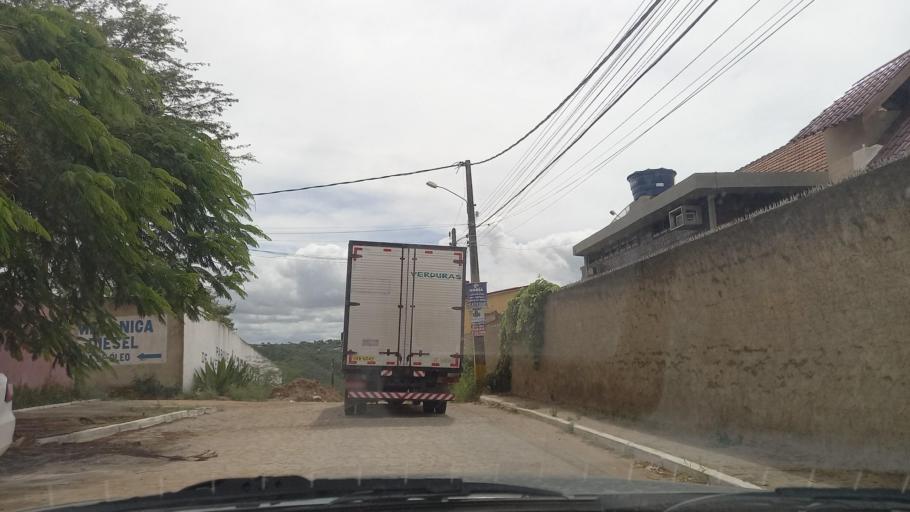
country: BR
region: Pernambuco
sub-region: Gravata
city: Gravata
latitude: -8.1944
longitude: -35.5622
